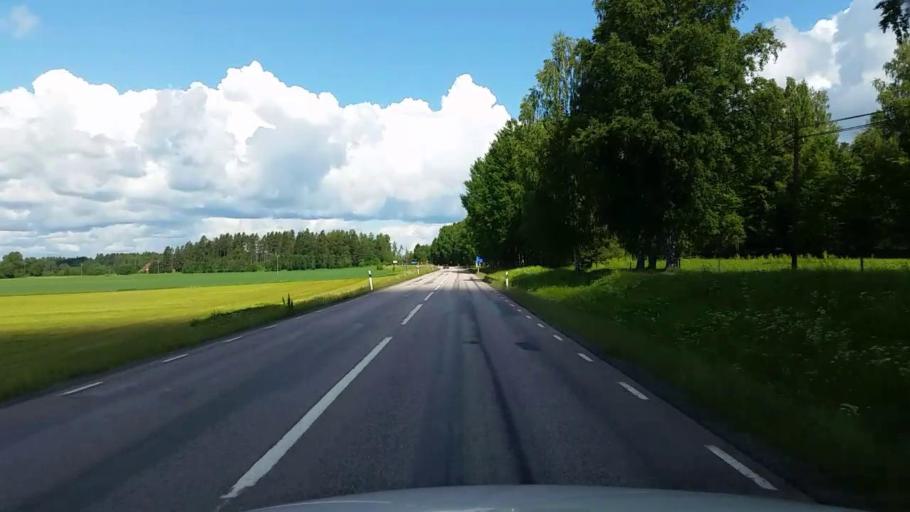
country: SE
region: Vaestmanland
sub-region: Kopings Kommun
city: Kolsva
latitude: 59.6770
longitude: 15.7663
